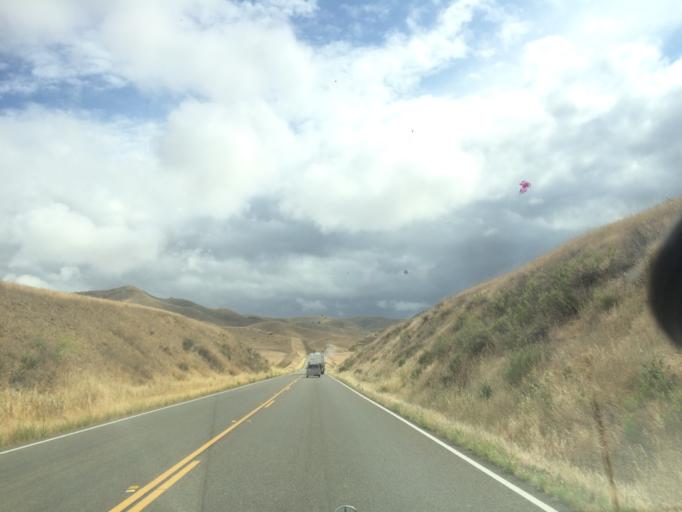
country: US
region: California
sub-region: San Luis Obispo County
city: Shandon
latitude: 35.7738
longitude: -120.2305
